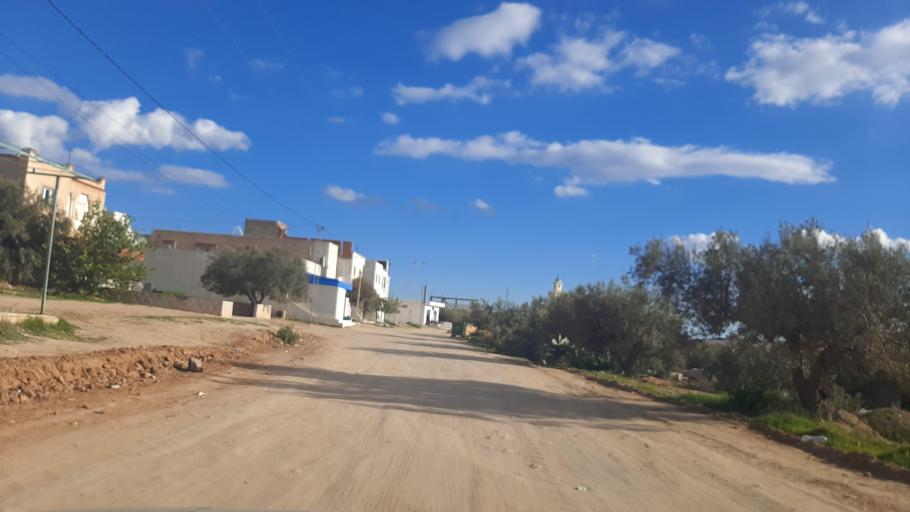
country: TN
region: Nabul
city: Al Hammamat
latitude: 36.4184
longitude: 10.5139
